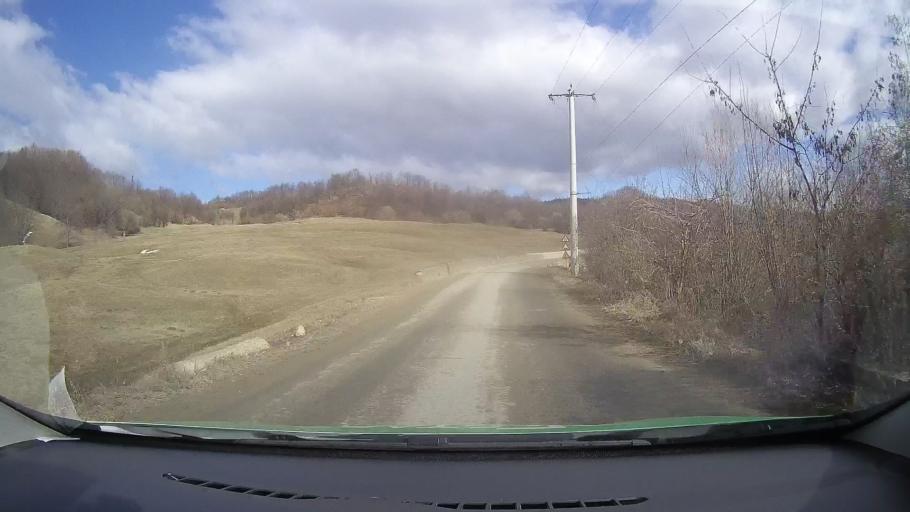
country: RO
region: Dambovita
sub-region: Comuna Motaeni
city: Motaeni
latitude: 45.1130
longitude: 25.4426
